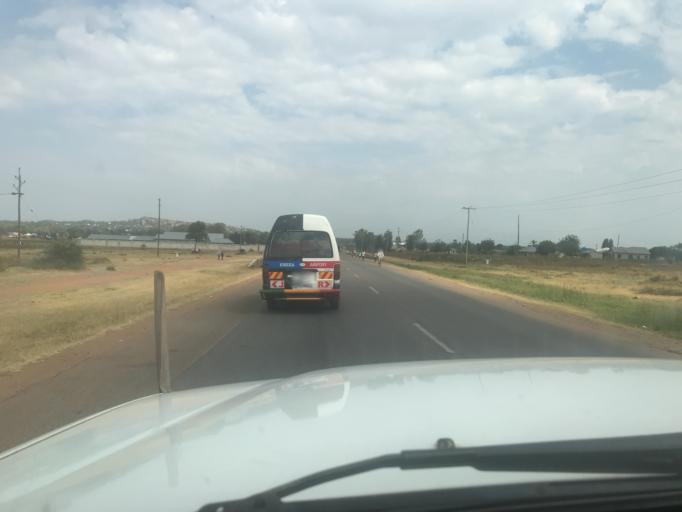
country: TZ
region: Mwanza
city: Mwanza
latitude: -2.5502
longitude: 33.0084
